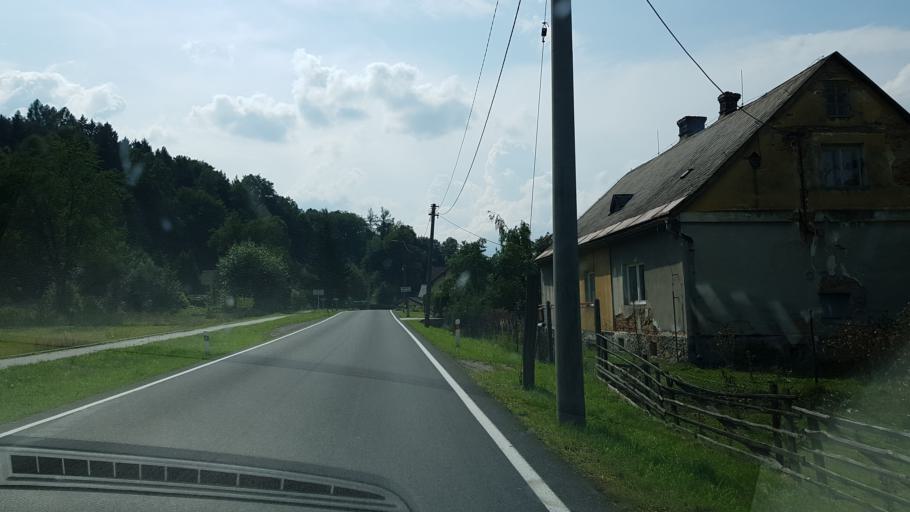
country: CZ
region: Olomoucky
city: Mikulovice
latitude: 50.2826
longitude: 17.2897
